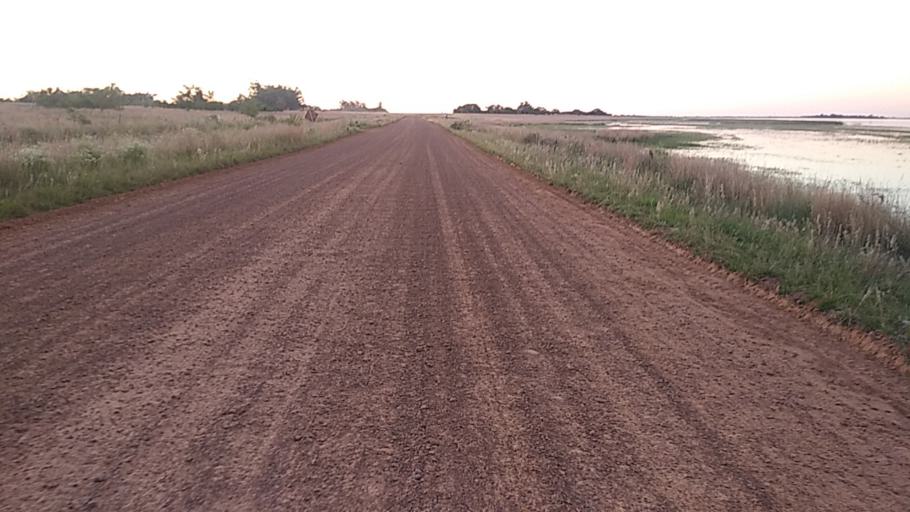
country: AR
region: Corrientes
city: Yataity Calle
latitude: -29.0105
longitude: -58.9121
